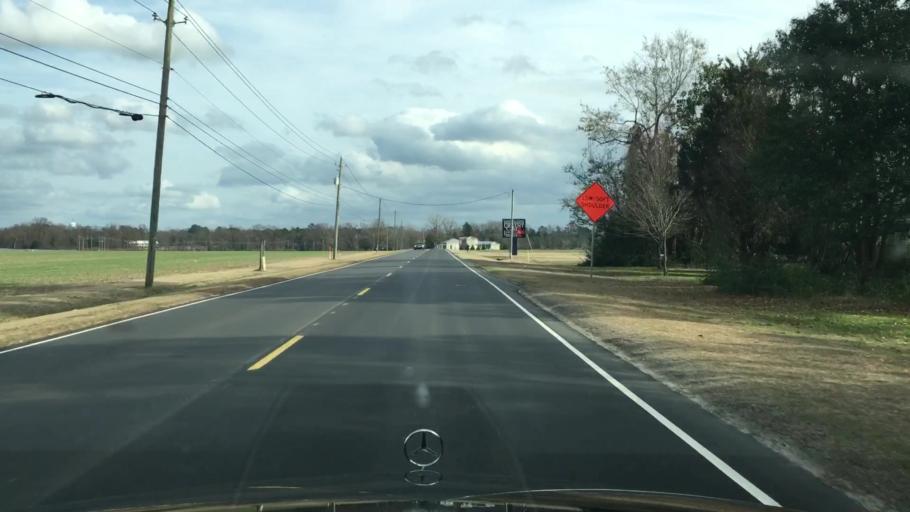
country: US
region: North Carolina
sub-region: Duplin County
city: Kenansville
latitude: 34.9596
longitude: -77.9866
